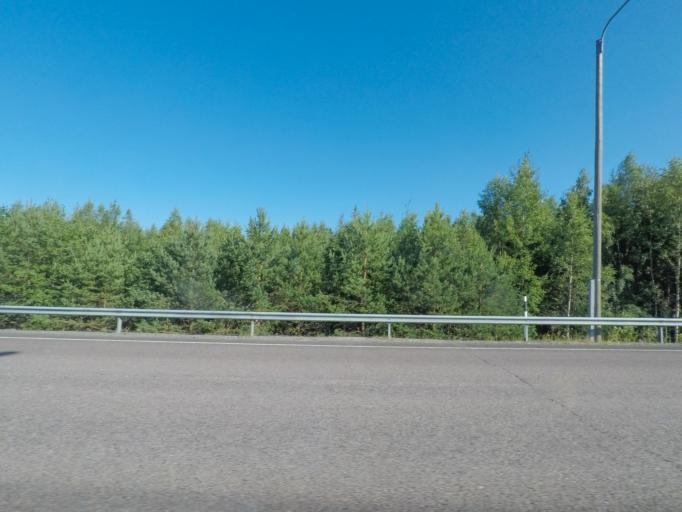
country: FI
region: Paijanne Tavastia
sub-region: Lahti
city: Heinola
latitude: 61.3314
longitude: 26.1635
